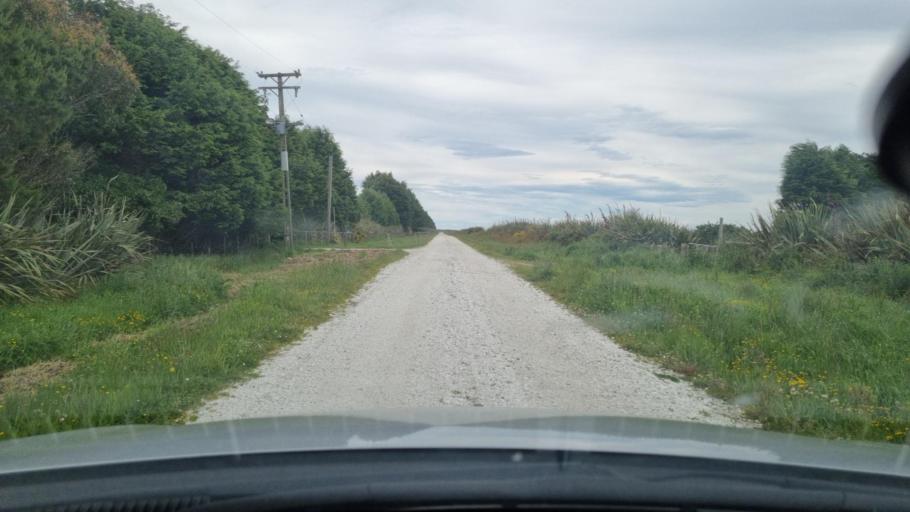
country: NZ
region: Southland
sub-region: Invercargill City
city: Bluff
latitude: -46.5138
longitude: 168.3561
